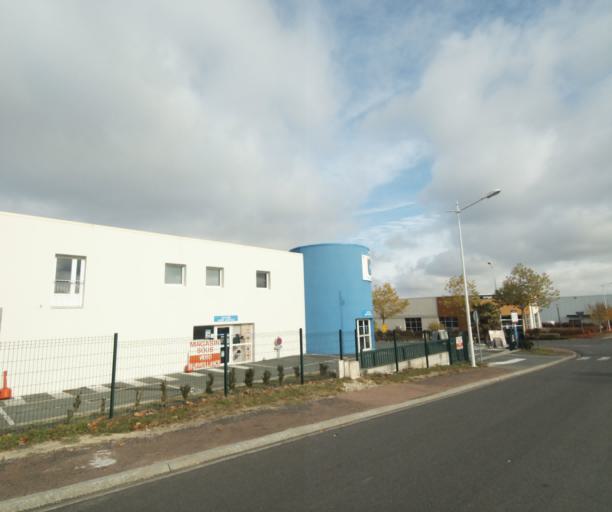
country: FR
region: Poitou-Charentes
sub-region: Departement de la Charente-Maritime
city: Saint-Georges-des-Coteaux
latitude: 45.7505
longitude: -0.6786
